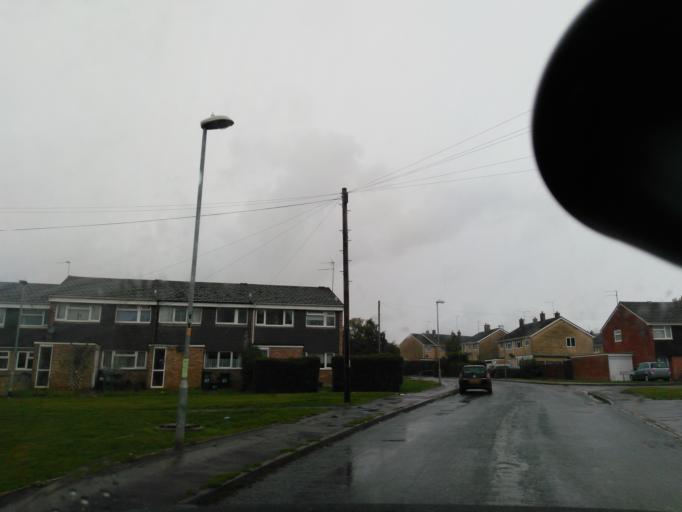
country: GB
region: England
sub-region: Wiltshire
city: Chippenham
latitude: 51.4555
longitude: -2.1409
